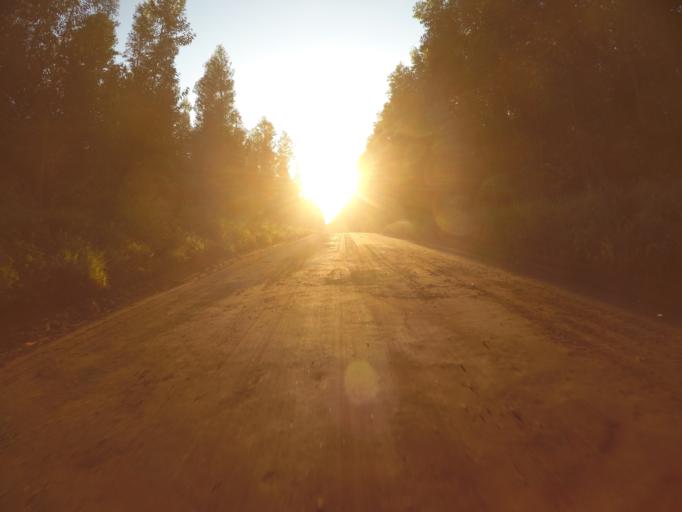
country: ZA
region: KwaZulu-Natal
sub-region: uThungulu District Municipality
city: KwaMbonambi
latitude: -28.6750
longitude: 32.1126
